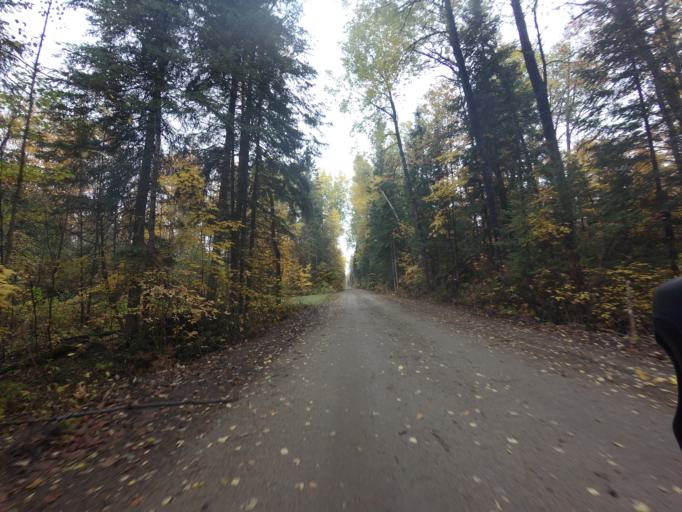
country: CA
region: Ontario
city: Renfrew
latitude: 45.1791
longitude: -76.6834
